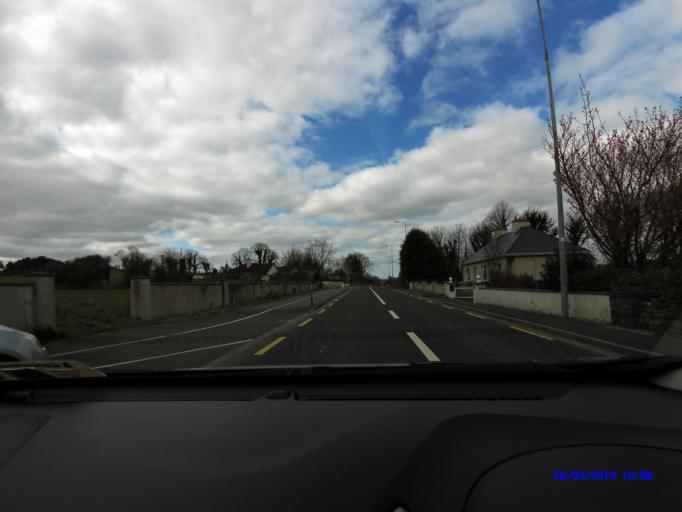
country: IE
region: Connaught
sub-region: Maigh Eo
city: Castlebar
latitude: 53.8546
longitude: -9.3306
